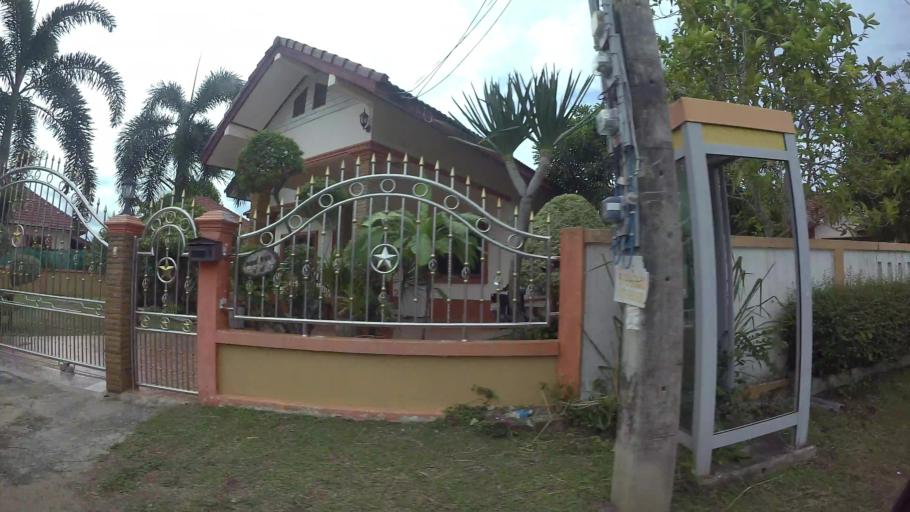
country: TH
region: Chon Buri
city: Sattahip
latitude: 12.7100
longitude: 100.8955
